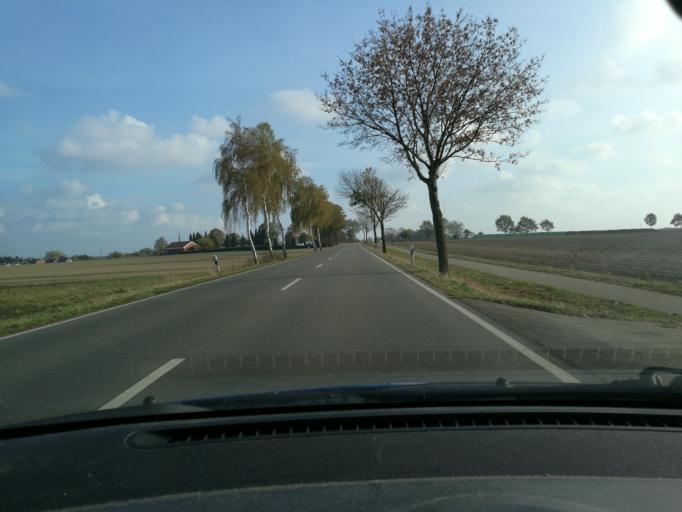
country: DE
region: Lower Saxony
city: Luechow
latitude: 52.9870
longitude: 11.1231
